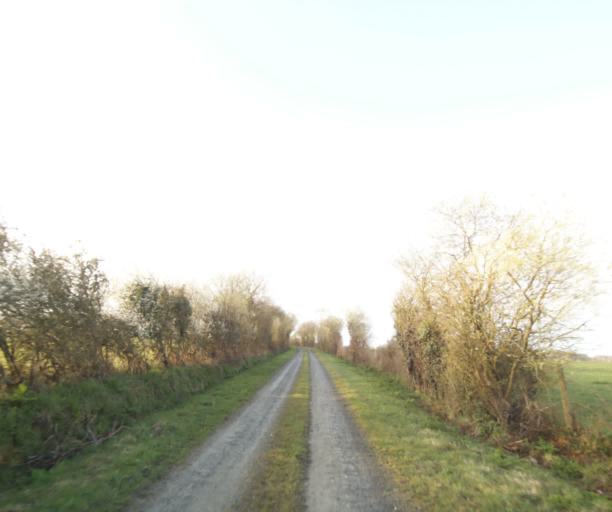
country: FR
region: Pays de la Loire
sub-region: Departement de la Loire-Atlantique
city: Savenay
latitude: 47.3909
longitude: -1.9144
